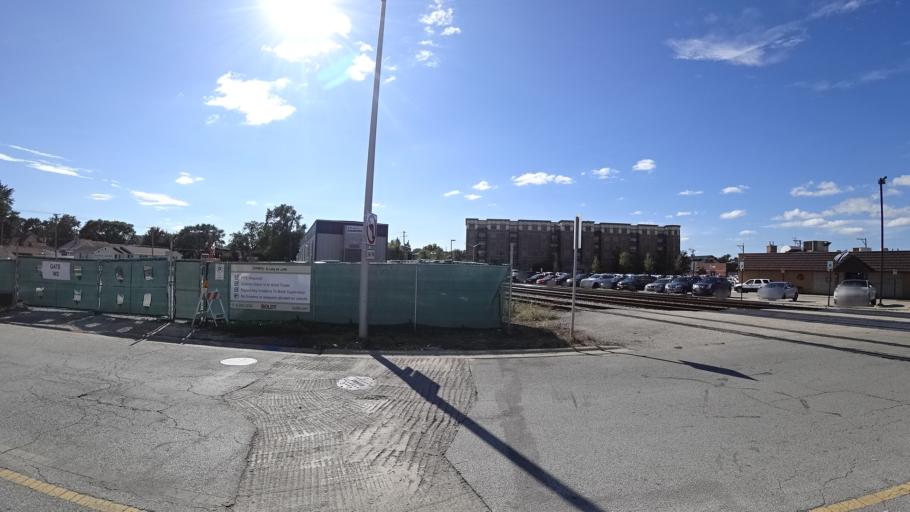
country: US
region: Illinois
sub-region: Cook County
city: Oak Lawn
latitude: 41.7186
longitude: -87.7505
